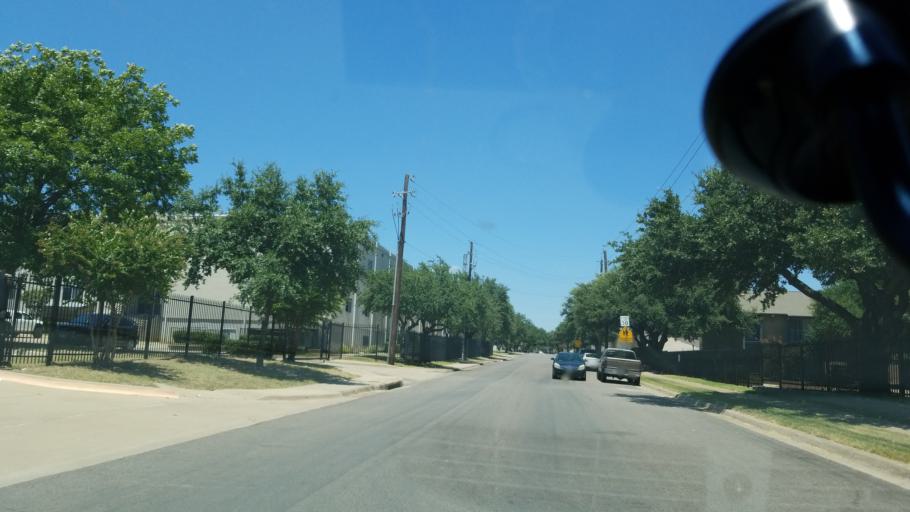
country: US
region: Texas
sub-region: Dallas County
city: Cockrell Hill
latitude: 32.6998
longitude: -96.8301
